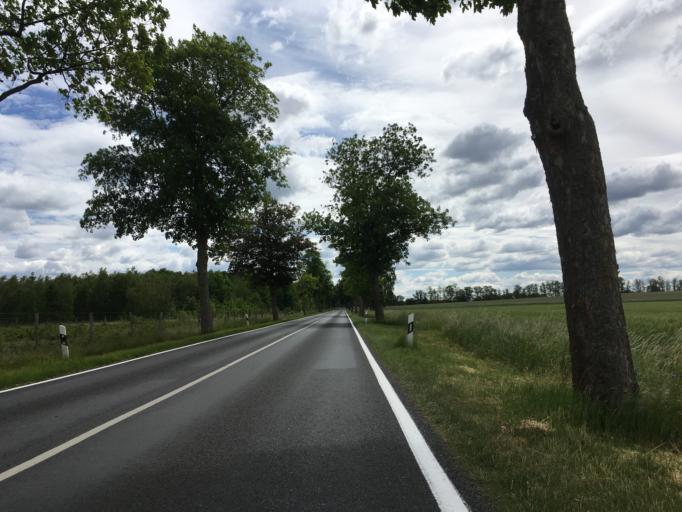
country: DE
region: Brandenburg
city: Melchow
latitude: 52.7486
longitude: 13.6882
